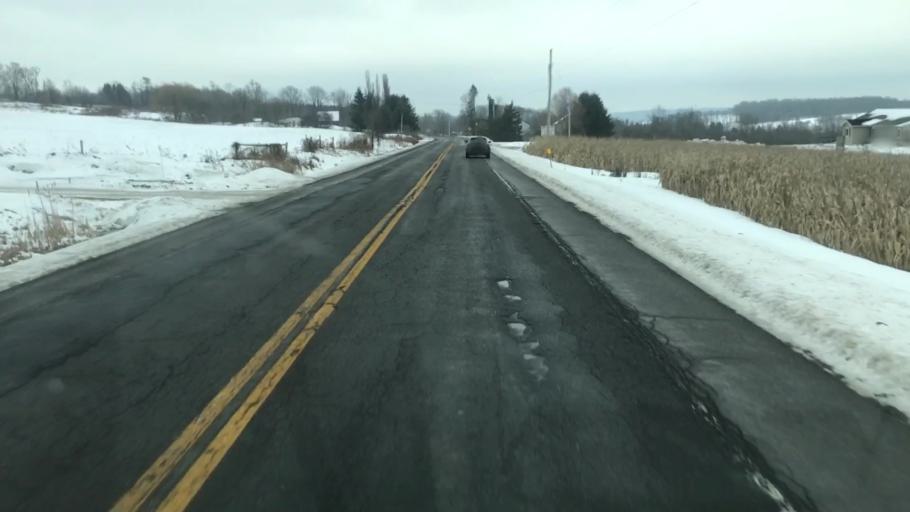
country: US
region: New York
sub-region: Cayuga County
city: Moravia
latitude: 42.7396
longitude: -76.3164
